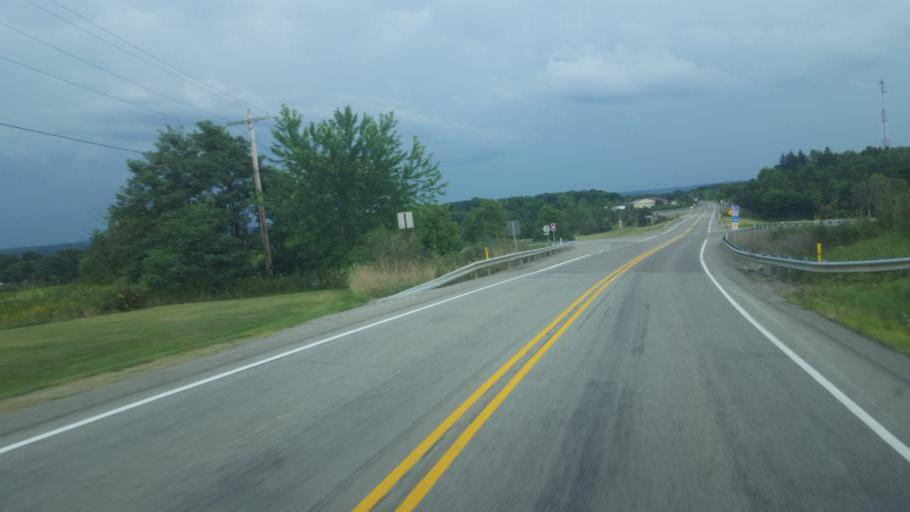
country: US
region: Pennsylvania
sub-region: Clarion County
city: Knox
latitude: 41.1871
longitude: -79.5421
